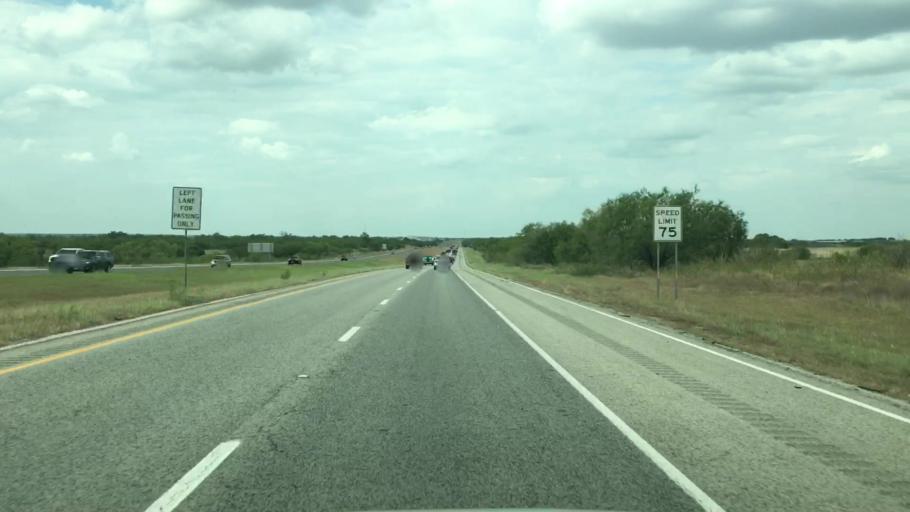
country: US
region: Texas
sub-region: Atascosa County
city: Pleasanton
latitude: 29.0654
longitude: -98.4327
